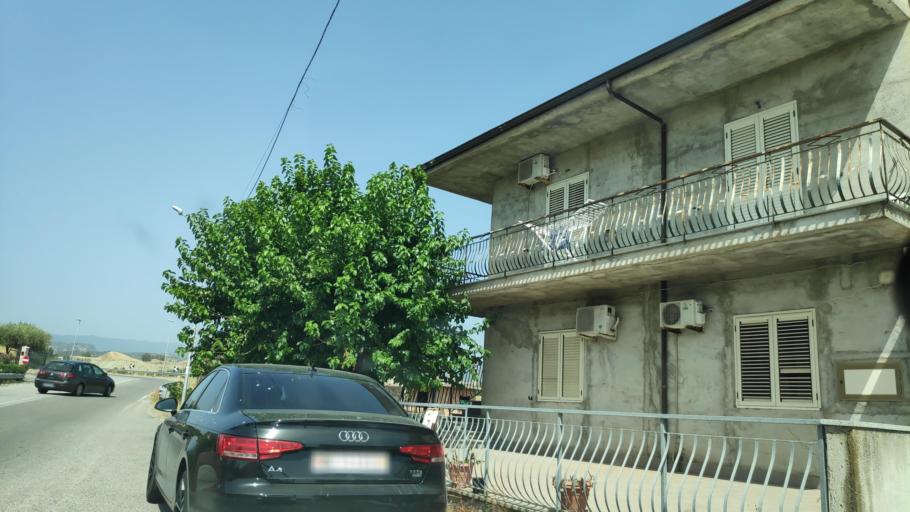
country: IT
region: Calabria
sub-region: Provincia di Catanzaro
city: Guardavalle Marina
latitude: 38.4849
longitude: 16.5712
